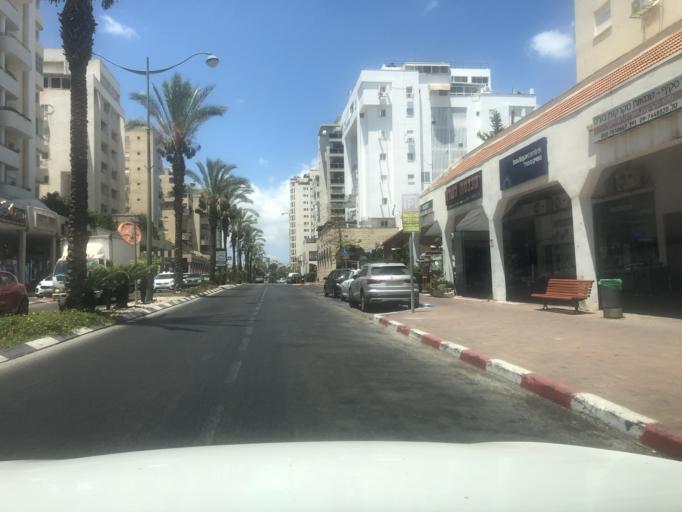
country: IL
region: Central District
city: Hod HaSharon
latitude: 32.1613
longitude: 34.9029
